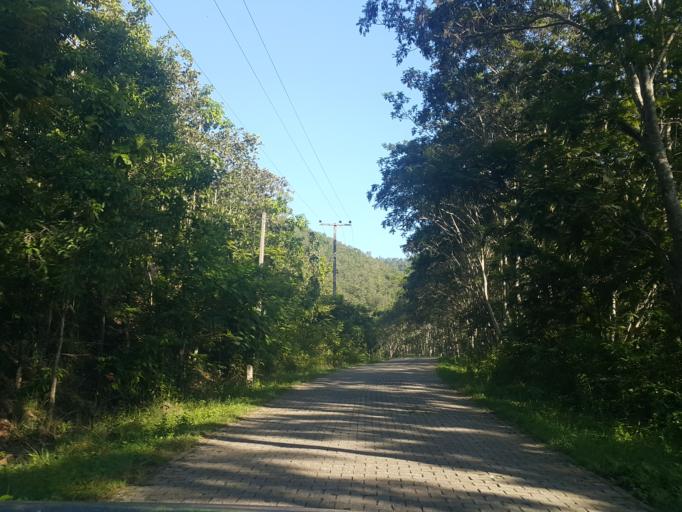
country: TH
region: Chiang Mai
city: Mae On
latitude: 18.7096
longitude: 99.2046
